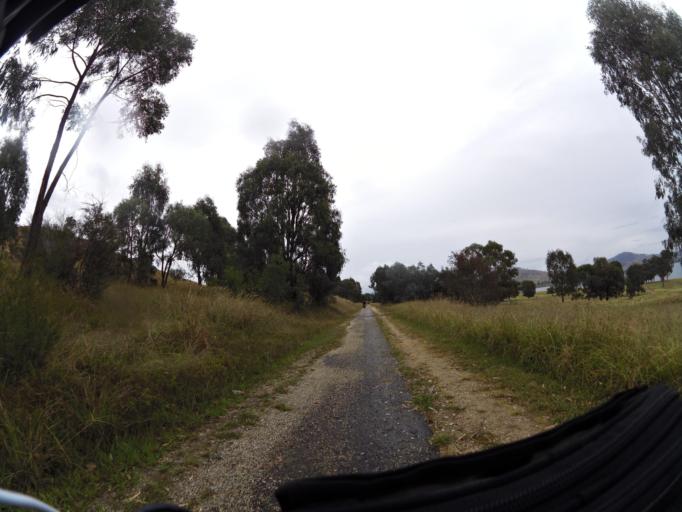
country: AU
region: New South Wales
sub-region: Albury Municipality
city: East Albury
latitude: -36.2243
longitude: 147.1076
